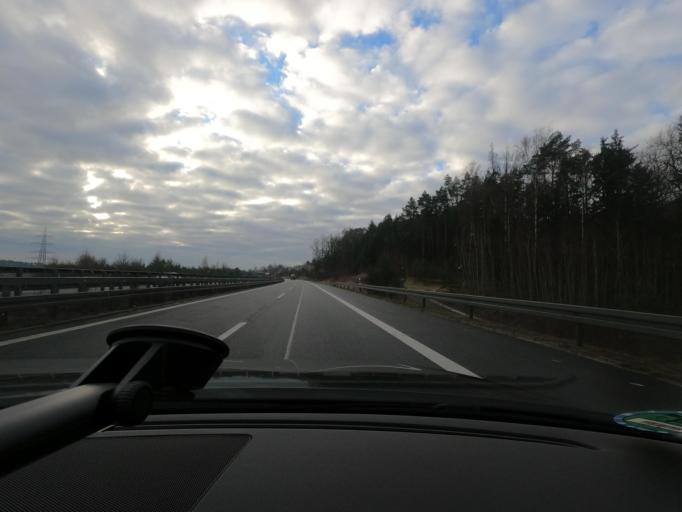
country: DE
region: Bavaria
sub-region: Upper Franconia
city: Rodental
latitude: 50.2660
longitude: 11.0173
